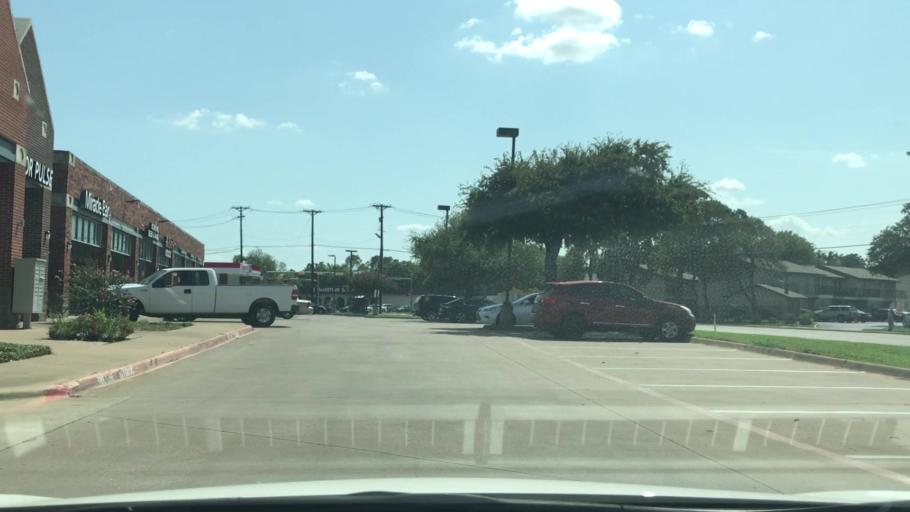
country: US
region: Texas
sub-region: Dallas County
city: Irving
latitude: 32.8455
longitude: -96.9505
